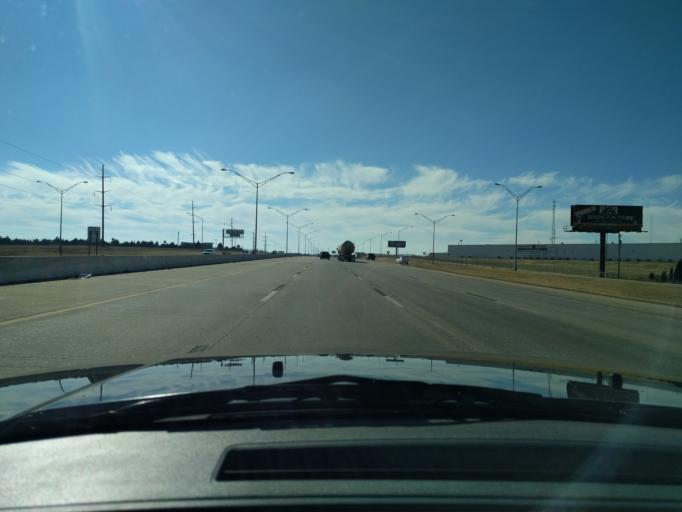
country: US
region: Oklahoma
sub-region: Oklahoma County
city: The Village
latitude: 35.5922
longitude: -97.5094
